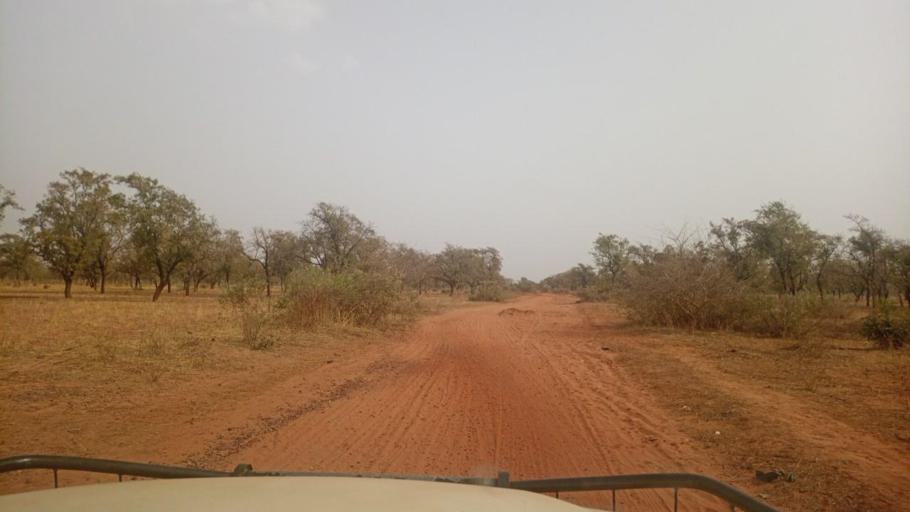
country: BF
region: Boucle du Mouhoun
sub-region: Province des Banwa
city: Salanso
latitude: 12.1056
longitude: -4.3351
